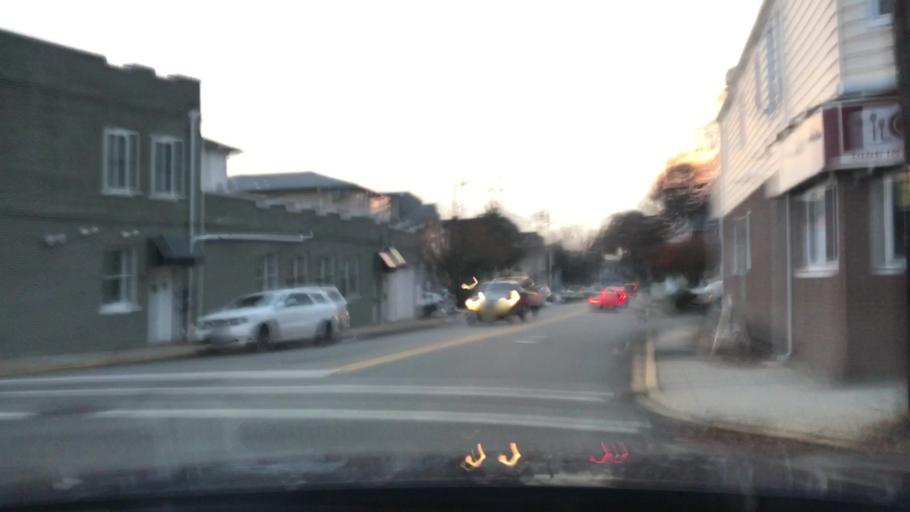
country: US
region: New Jersey
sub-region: Bergen County
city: Wallington
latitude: 40.8499
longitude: -74.1143
